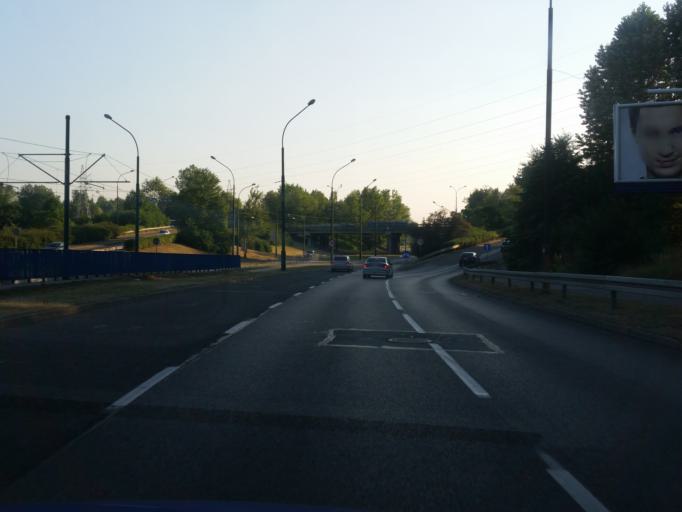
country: PL
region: Silesian Voivodeship
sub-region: Powiat bedzinski
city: Bedzin
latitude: 50.2955
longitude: 19.1700
